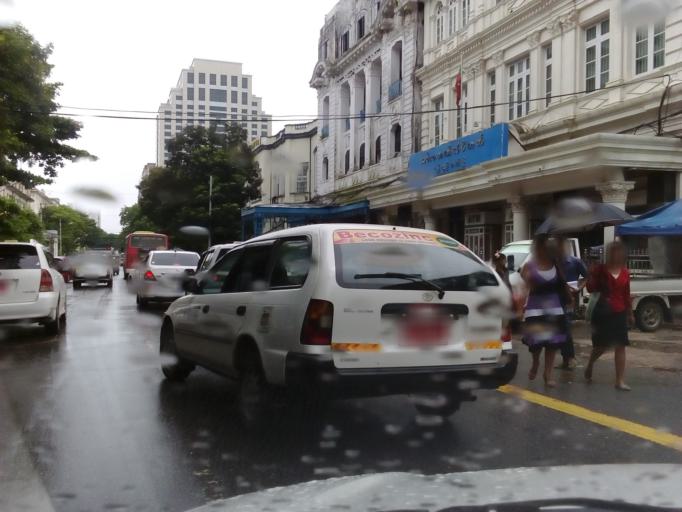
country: MM
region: Yangon
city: Yangon
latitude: 16.7718
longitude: 96.1612
